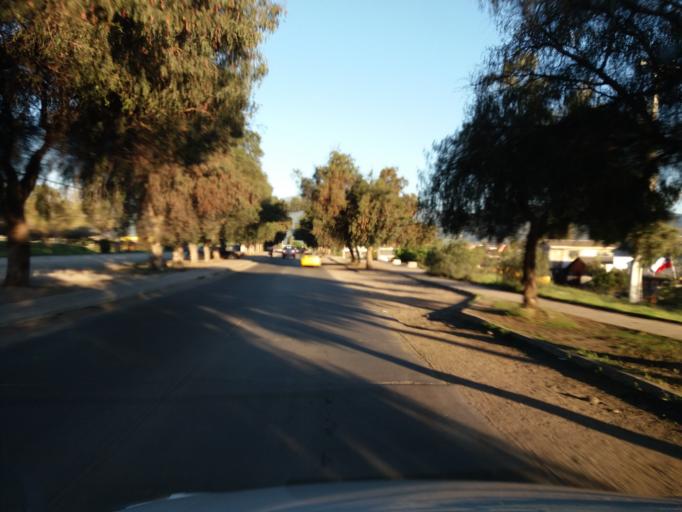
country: CL
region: Valparaiso
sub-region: Provincia de Quillota
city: Quillota
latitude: -32.8781
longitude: -71.2630
